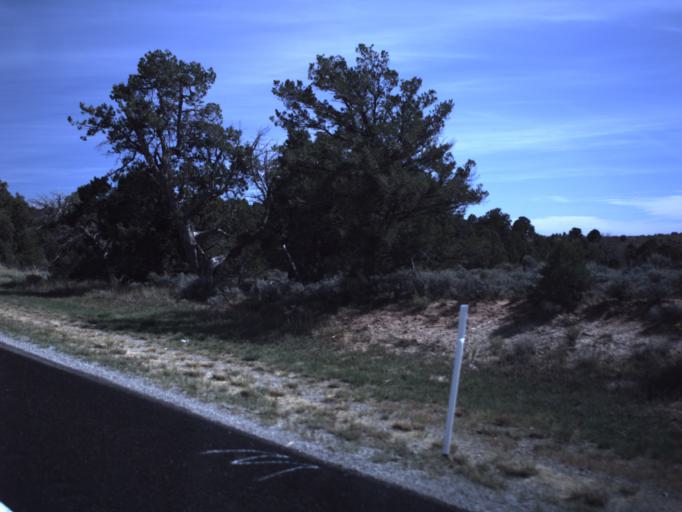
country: US
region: Utah
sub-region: San Juan County
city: Monticello
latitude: 37.8605
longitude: -109.2097
